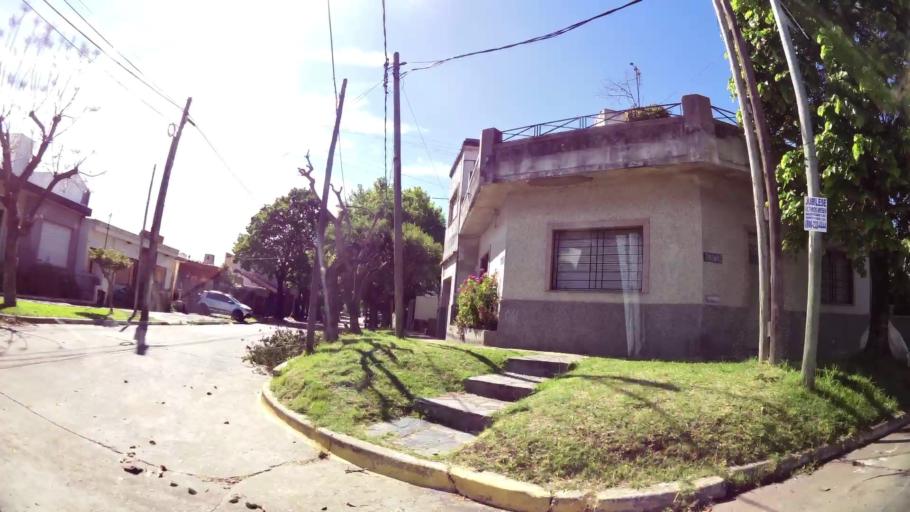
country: AR
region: Buenos Aires
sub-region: Partido de Quilmes
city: Quilmes
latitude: -34.7015
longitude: -58.2898
